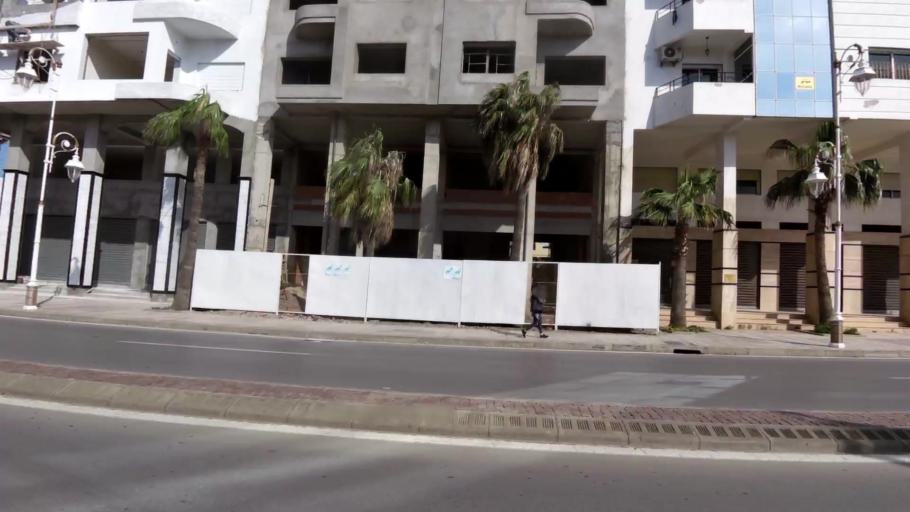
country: MA
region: Tanger-Tetouan
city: Tetouan
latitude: 35.5906
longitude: -5.3450
